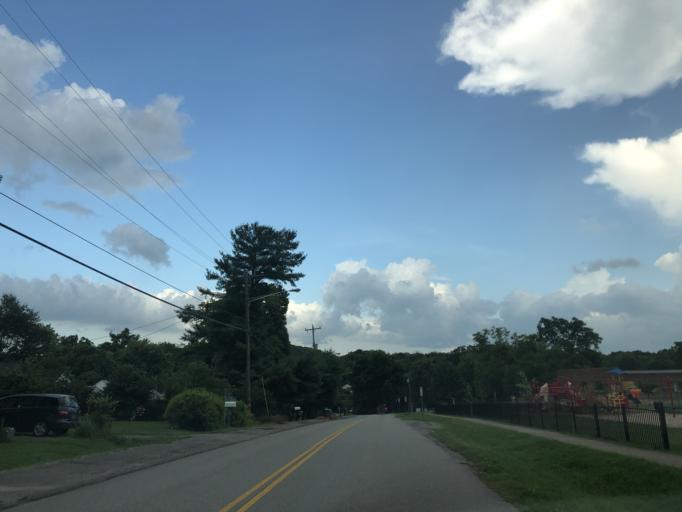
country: US
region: Tennessee
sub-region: Davidson County
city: Lakewood
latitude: 36.1774
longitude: -86.6828
